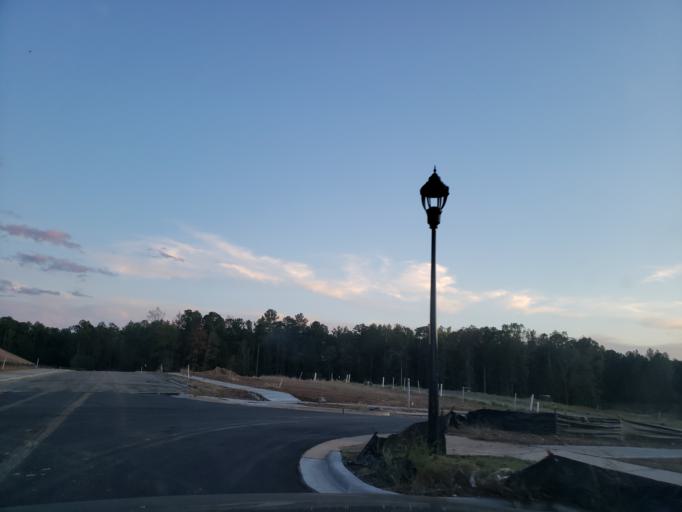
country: US
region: North Carolina
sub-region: Orange County
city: Chapel Hill
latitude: 35.8778
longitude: -78.9543
